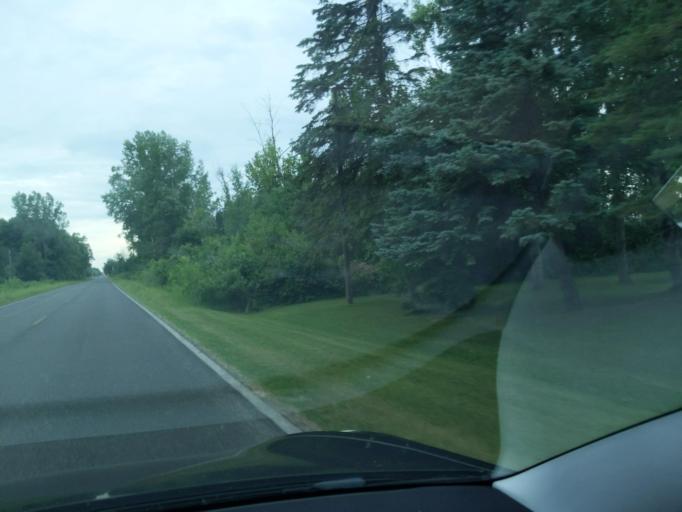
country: US
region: Michigan
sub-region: Isabella County
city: Mount Pleasant
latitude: 43.6185
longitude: -84.7278
